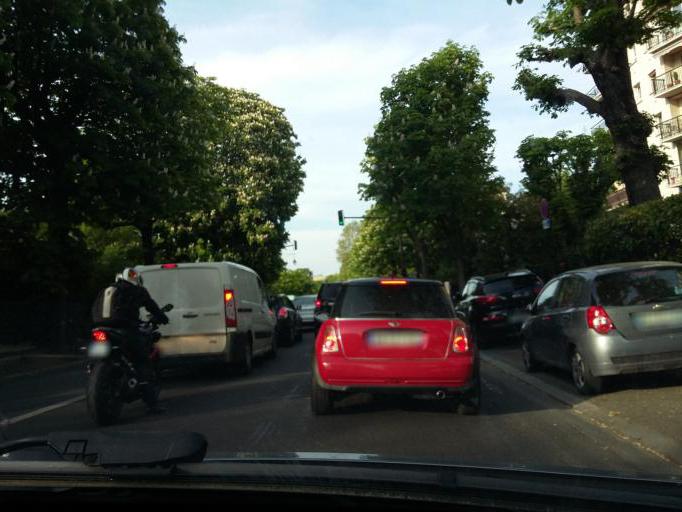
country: FR
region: Ile-de-France
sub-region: Departement des Hauts-de-Seine
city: Puteaux
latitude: 48.8797
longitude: 2.2504
